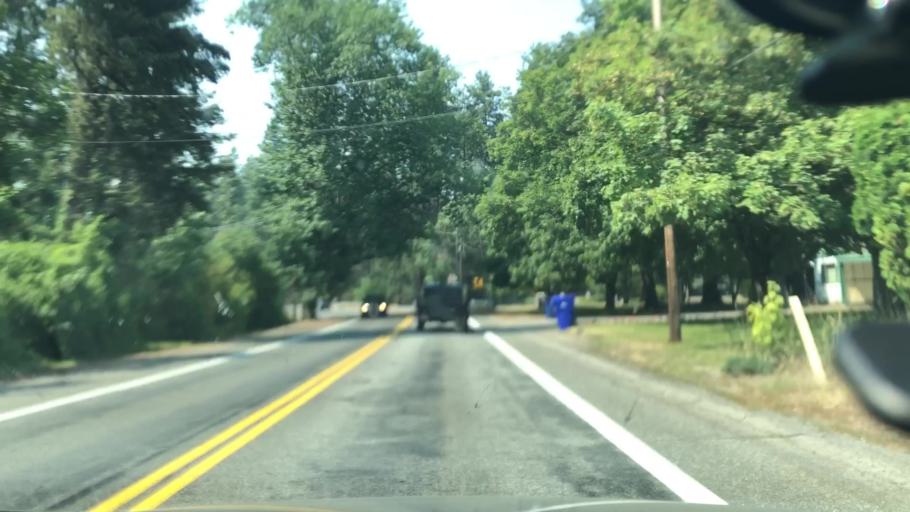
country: US
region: Washington
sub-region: Spokane County
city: Millwood
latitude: 47.6978
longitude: -117.2873
